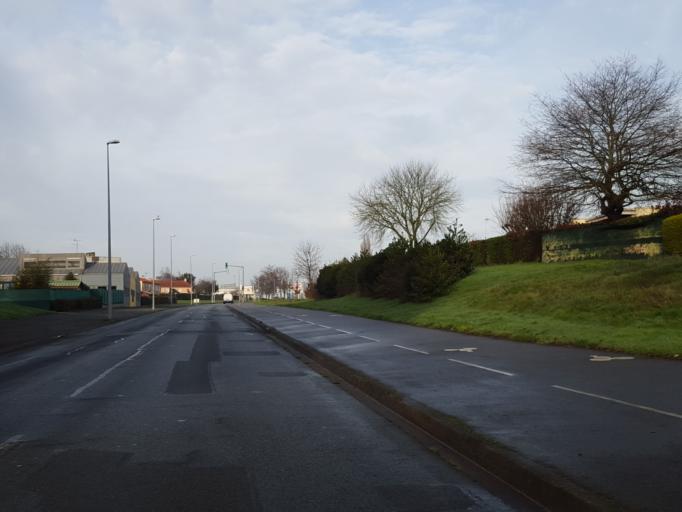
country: FR
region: Pays de la Loire
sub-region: Departement de la Vendee
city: La Roche-sur-Yon
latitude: 46.6819
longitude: -1.4242
